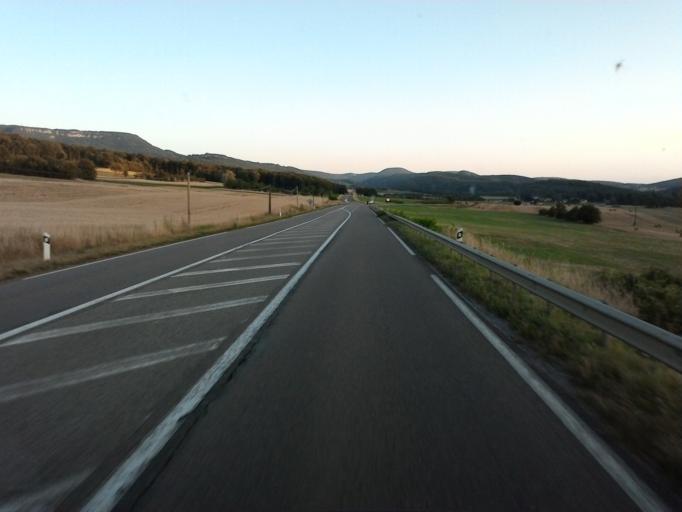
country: FR
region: Franche-Comte
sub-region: Departement du Jura
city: Salins-les-Bains
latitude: 47.0237
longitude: 5.8686
